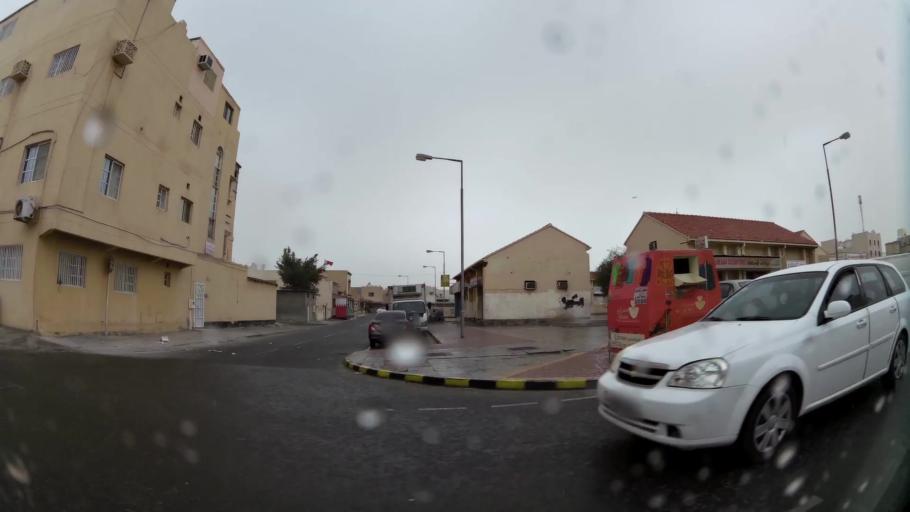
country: BH
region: Northern
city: Madinat `Isa
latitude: 26.1573
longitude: 50.5691
